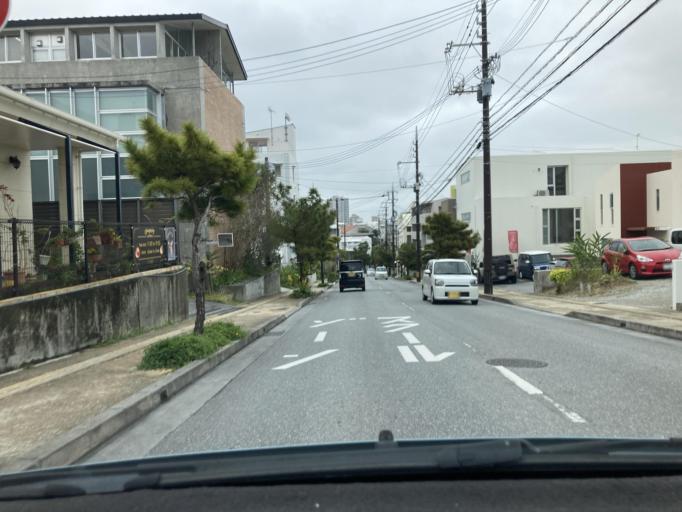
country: JP
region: Okinawa
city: Naha-shi
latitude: 26.2264
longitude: 127.6890
